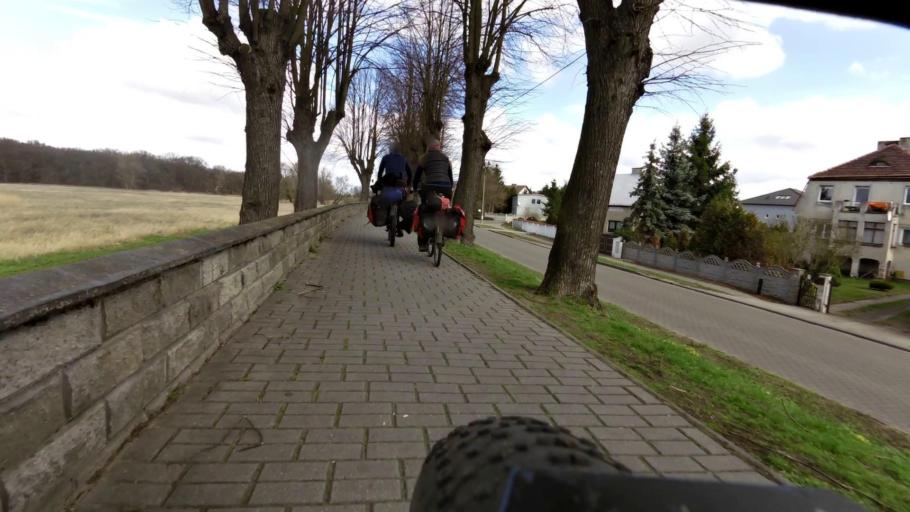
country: PL
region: Lubusz
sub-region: Powiat slubicki
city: Slubice
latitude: 52.3586
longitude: 14.5590
